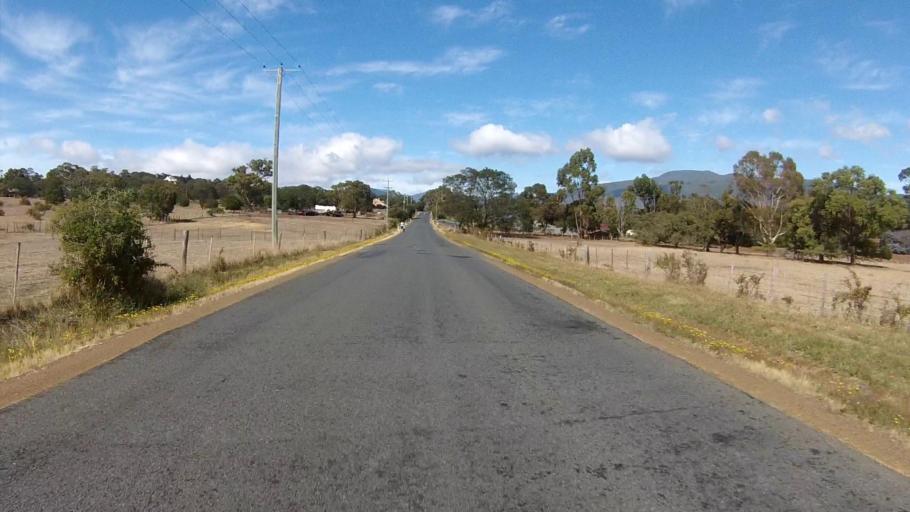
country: AU
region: Tasmania
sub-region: Brighton
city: Old Beach
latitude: -42.7653
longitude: 147.2762
